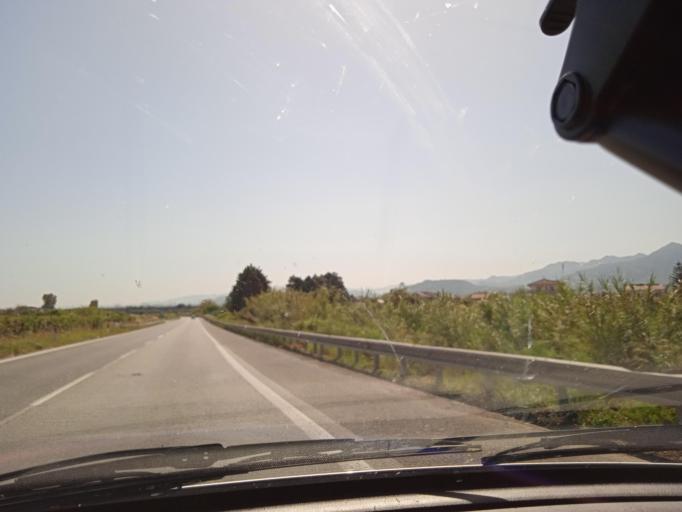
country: IT
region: Sicily
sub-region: Messina
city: Barcellona Pozzo di Gotto
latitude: 38.1637
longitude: 15.2043
